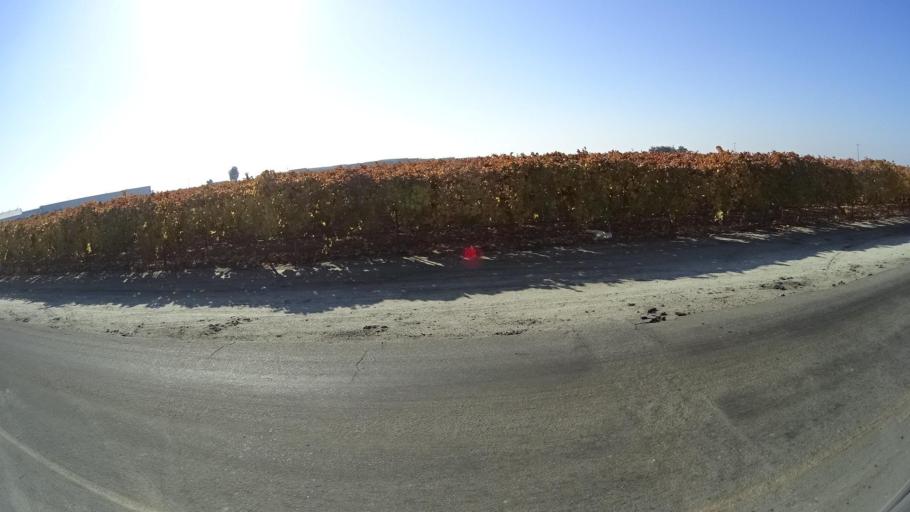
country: US
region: California
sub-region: Tulare County
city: Richgrove
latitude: 35.7471
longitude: -119.1451
